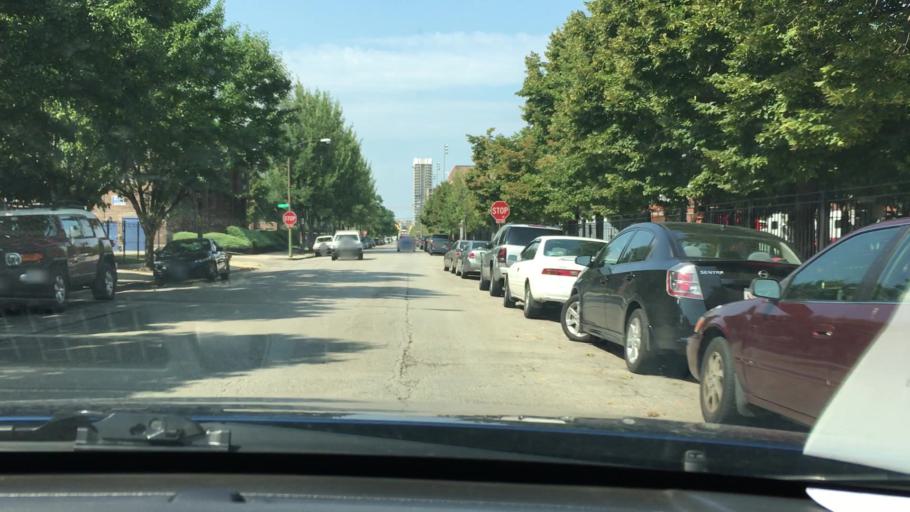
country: US
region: Illinois
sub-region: Cook County
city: Chicago
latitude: 41.8630
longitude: -87.6509
